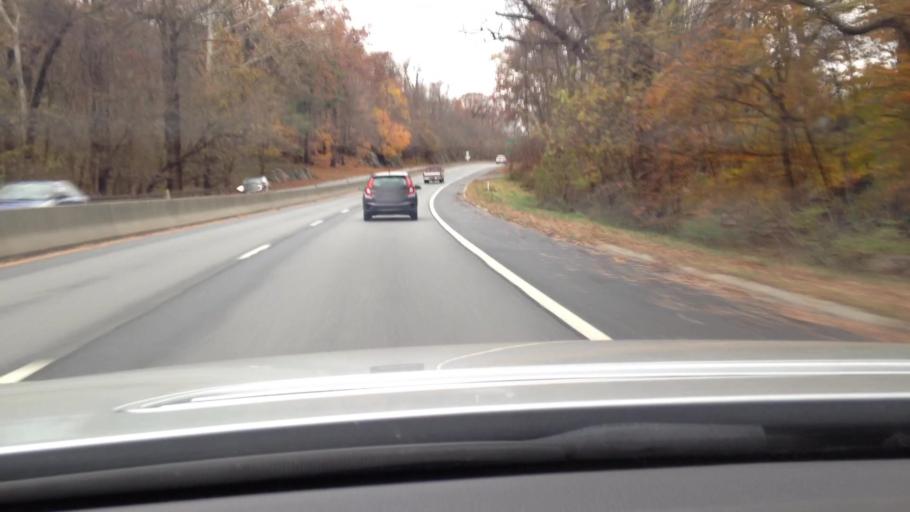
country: US
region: New York
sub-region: Westchester County
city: Elmsford
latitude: 41.0655
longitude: -73.8254
